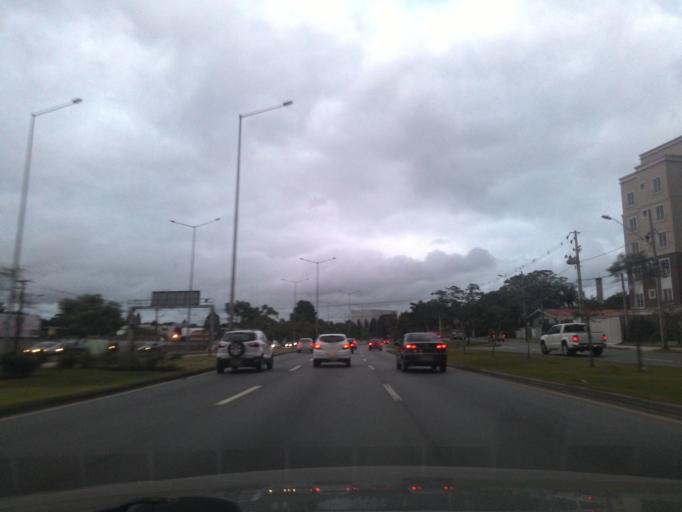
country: BR
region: Parana
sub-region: Curitiba
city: Curitiba
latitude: -25.4529
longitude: -49.2418
